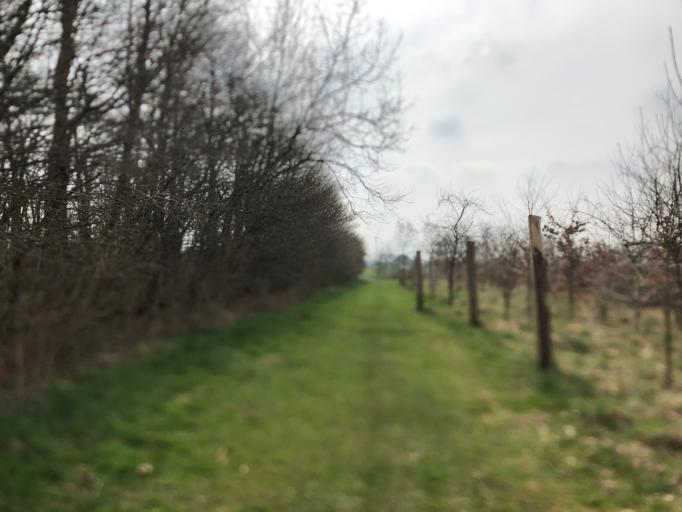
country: DE
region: Schleswig-Holstein
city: Wanderup
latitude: 54.6865
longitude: 9.3344
